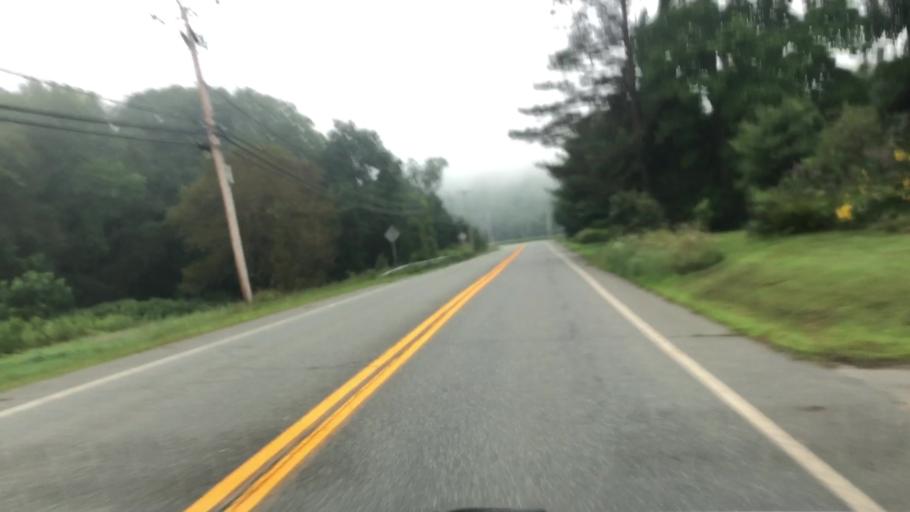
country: US
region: Massachusetts
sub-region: Franklin County
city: Buckland
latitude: 42.6120
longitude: -72.7709
